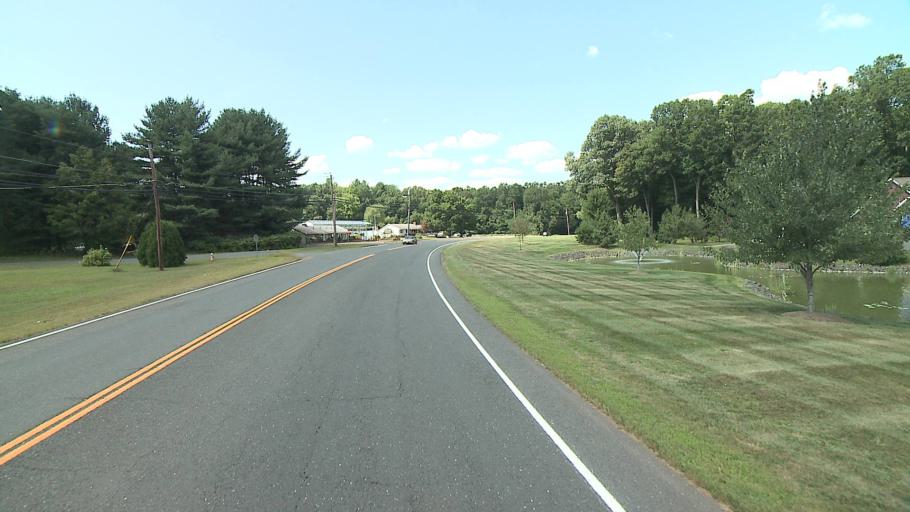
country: US
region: Connecticut
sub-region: Hartford County
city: Broad Brook
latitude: 41.9334
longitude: -72.5595
